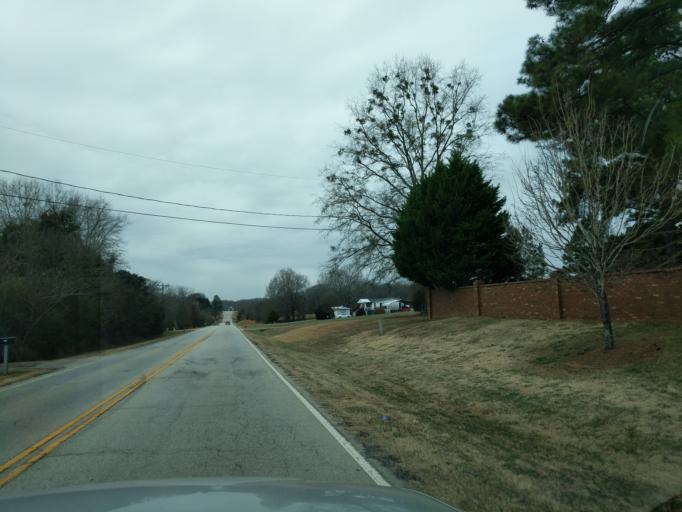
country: US
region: South Carolina
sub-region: Spartanburg County
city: Wellford
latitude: 34.8683
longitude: -82.0891
